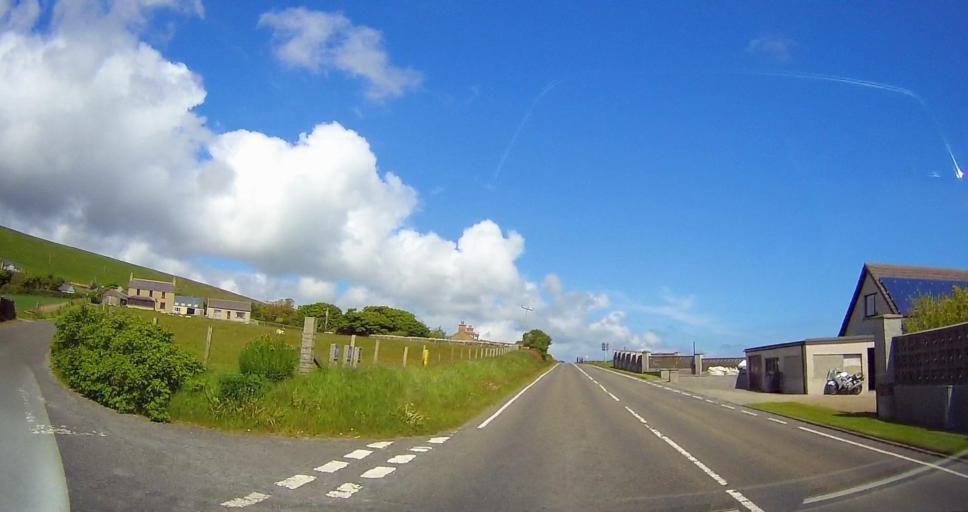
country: GB
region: Scotland
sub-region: Orkney Islands
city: Orkney
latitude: 59.0121
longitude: -3.1112
